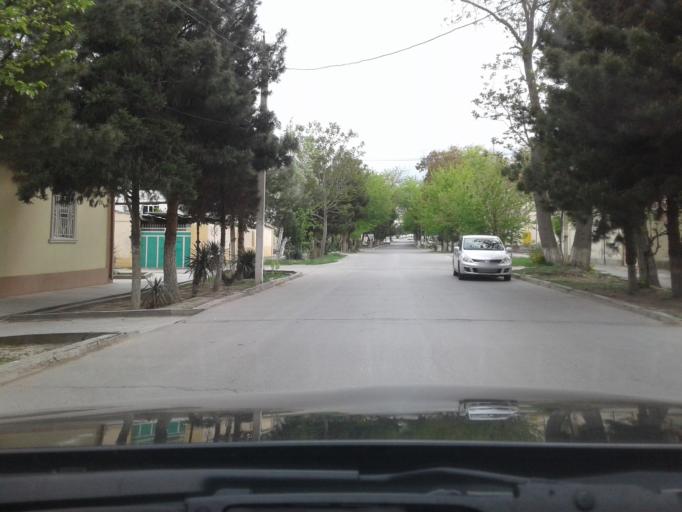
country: TM
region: Ahal
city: Ashgabat
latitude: 37.9471
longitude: 58.3575
